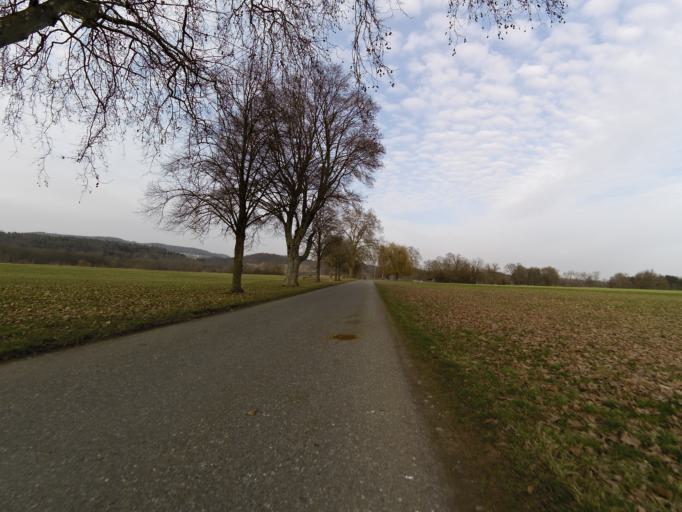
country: CH
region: Thurgau
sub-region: Frauenfeld District
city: Frauenfeld
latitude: 47.5768
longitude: 8.9110
